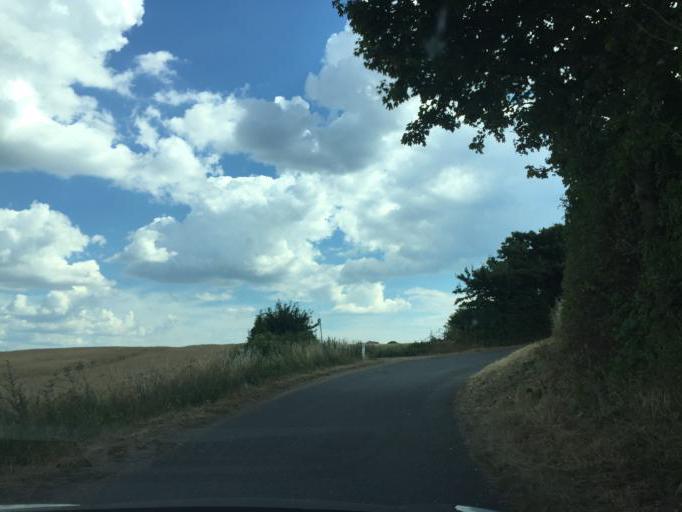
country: DK
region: South Denmark
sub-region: Assens Kommune
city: Glamsbjerg
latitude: 55.2121
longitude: 10.0074
